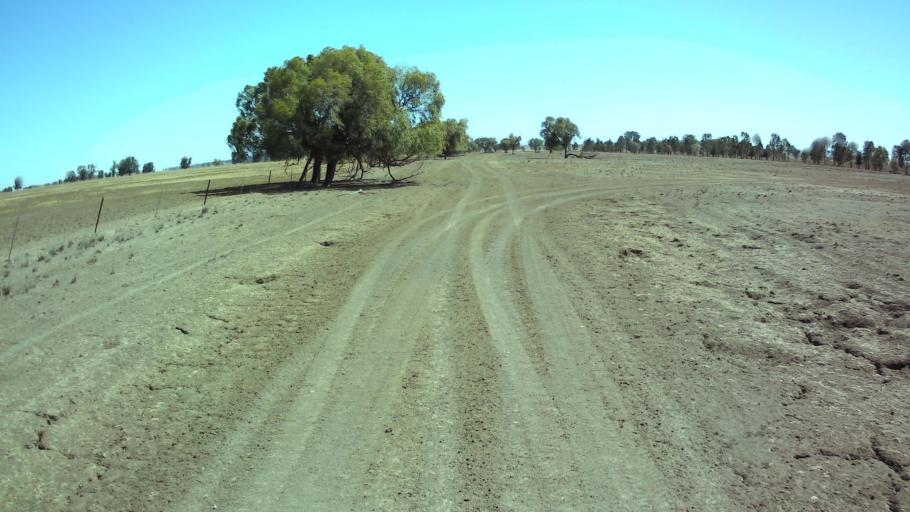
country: AU
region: New South Wales
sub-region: Forbes
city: Forbes
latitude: -33.7192
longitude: 147.6659
